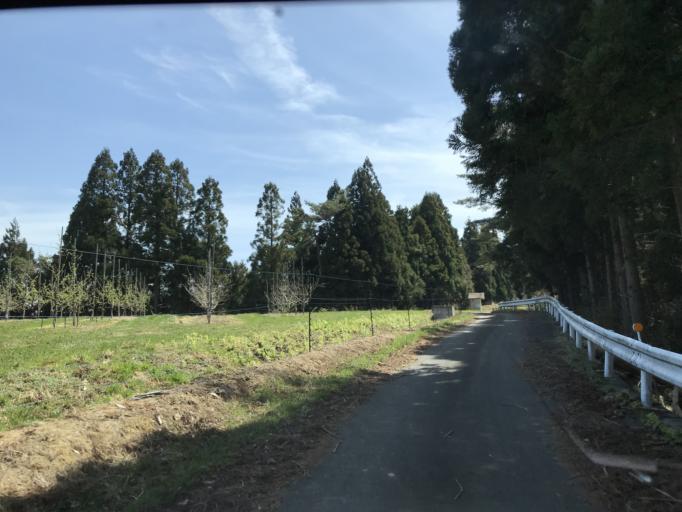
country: JP
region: Iwate
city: Ichinoseki
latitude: 38.8357
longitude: 141.2884
